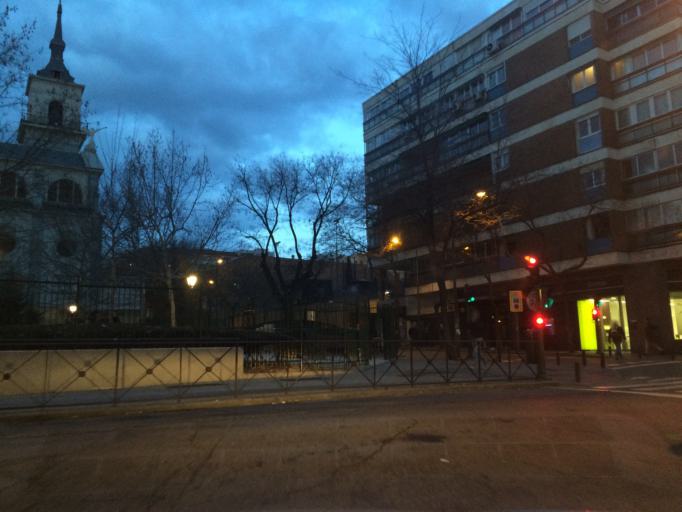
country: ES
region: Madrid
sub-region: Provincia de Madrid
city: Chamberi
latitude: 40.4328
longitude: -3.7119
